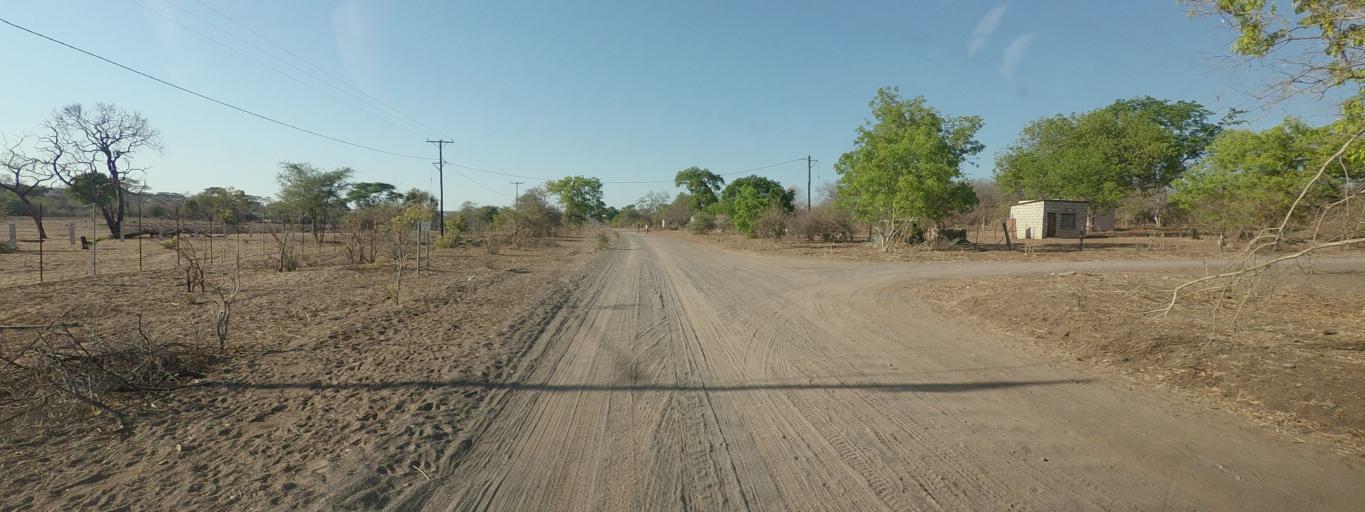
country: BW
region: North West
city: Kasane
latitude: -17.8921
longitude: 25.2292
